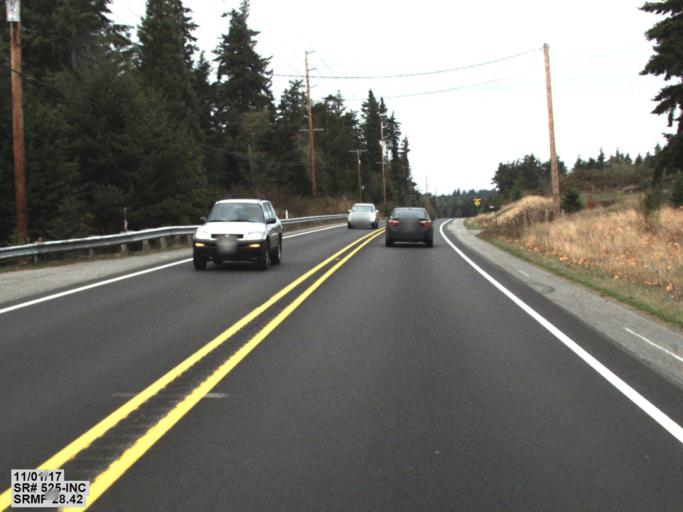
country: US
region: Washington
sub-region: Island County
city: Camano
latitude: 48.1438
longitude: -122.5933
